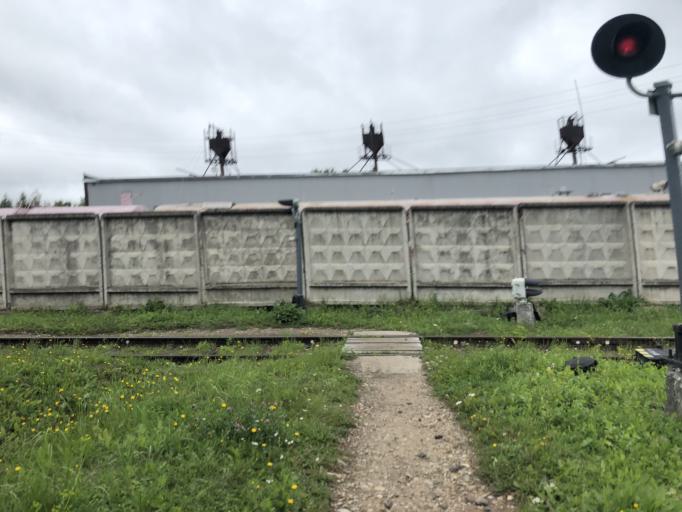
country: RU
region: Tverskaya
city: Rzhev
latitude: 56.2393
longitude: 34.3354
